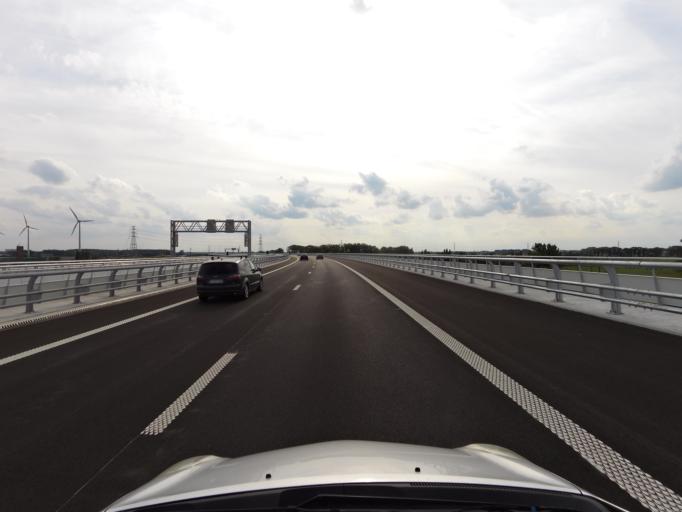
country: BE
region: Flanders
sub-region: Provincie West-Vlaanderen
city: Zuienkerke
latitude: 51.2724
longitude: 3.2080
